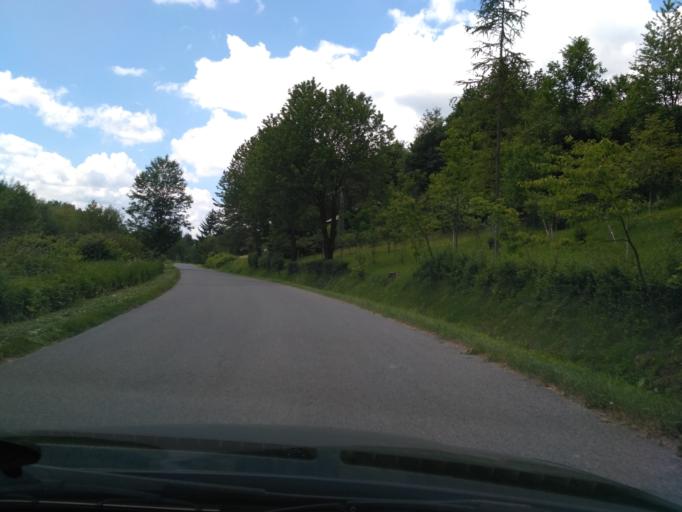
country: PL
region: Subcarpathian Voivodeship
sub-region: Powiat brzozowski
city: Wesola
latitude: 49.8096
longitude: 22.0548
